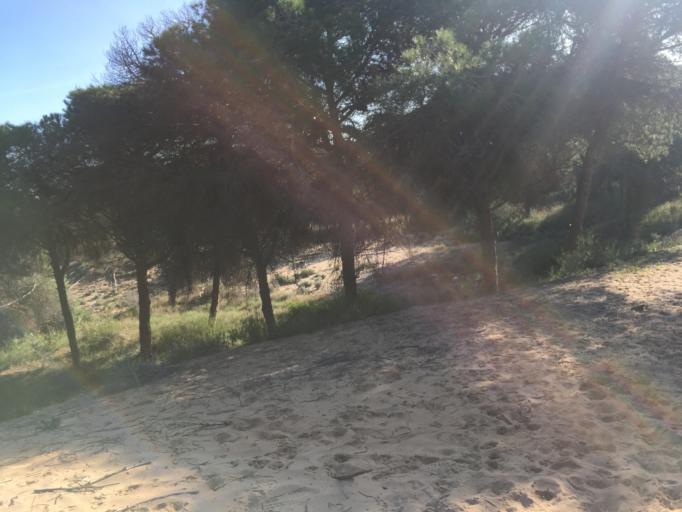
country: ES
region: Valencia
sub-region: Provincia de Alicante
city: Guardamar del Segura
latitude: 38.1315
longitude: -0.6429
